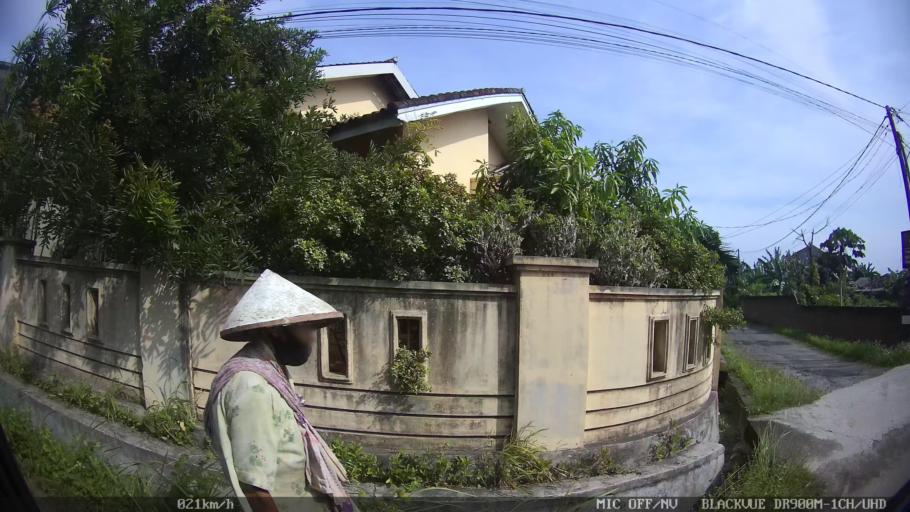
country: ID
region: Lampung
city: Kedaton
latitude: -5.3821
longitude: 105.2956
